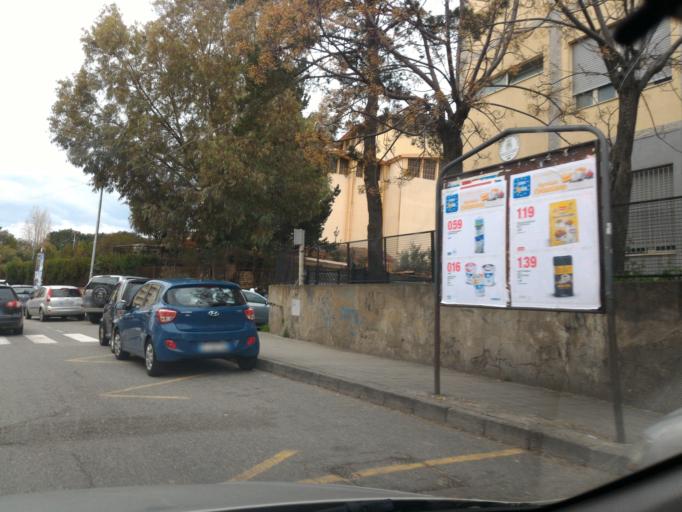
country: IT
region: Calabria
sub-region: Provincia di Catanzaro
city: Roccelletta
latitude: 38.8281
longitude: 16.6222
